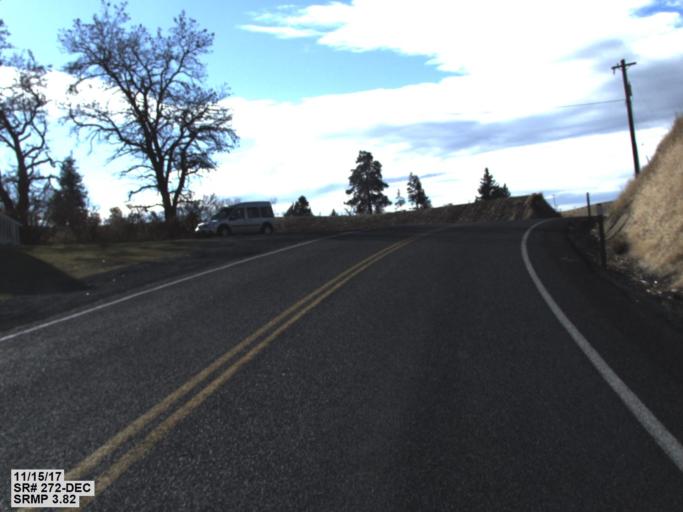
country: US
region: Washington
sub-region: Whitman County
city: Colfax
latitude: 46.9036
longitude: -117.2955
